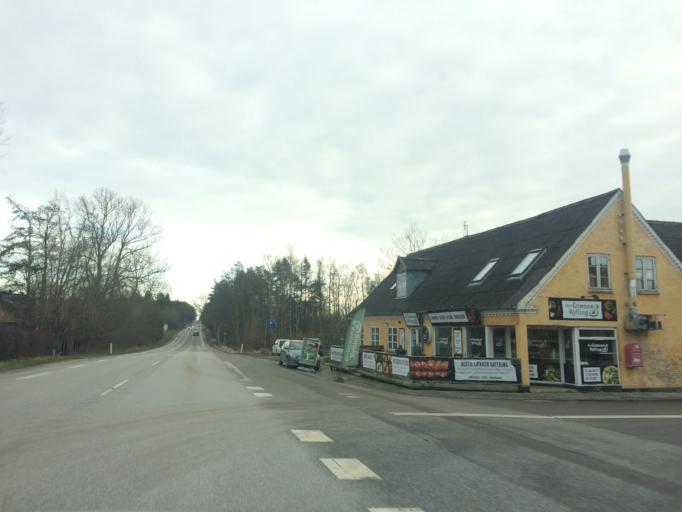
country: DK
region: Capital Region
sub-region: Fredensborg Kommune
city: Fredensborg
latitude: 55.9452
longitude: 12.4252
